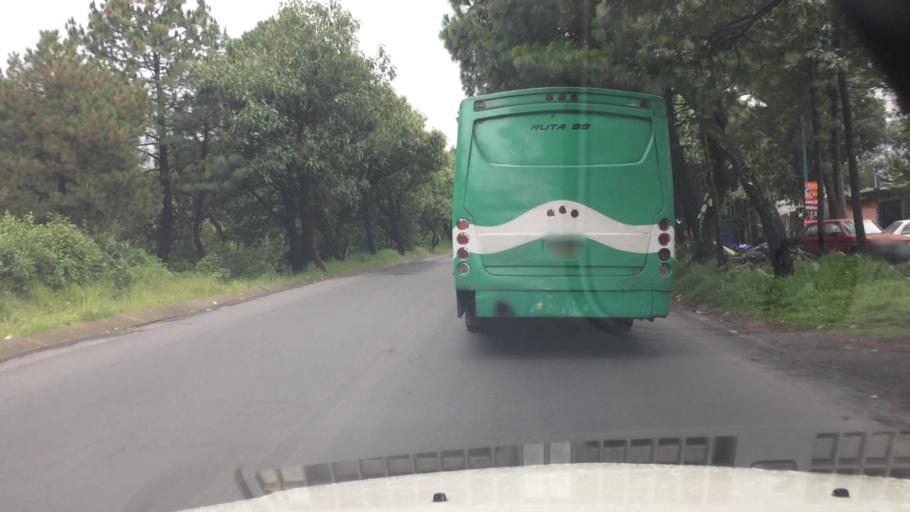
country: MX
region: Mexico City
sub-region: Tlalpan
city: Lomas de Tepemecatl
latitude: 19.2662
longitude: -99.2362
